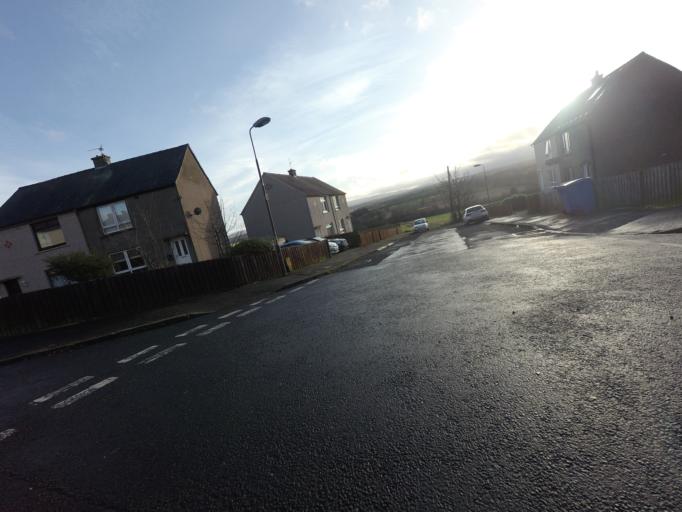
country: GB
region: Scotland
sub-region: West Lothian
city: West Calder
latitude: 55.8774
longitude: -3.5865
